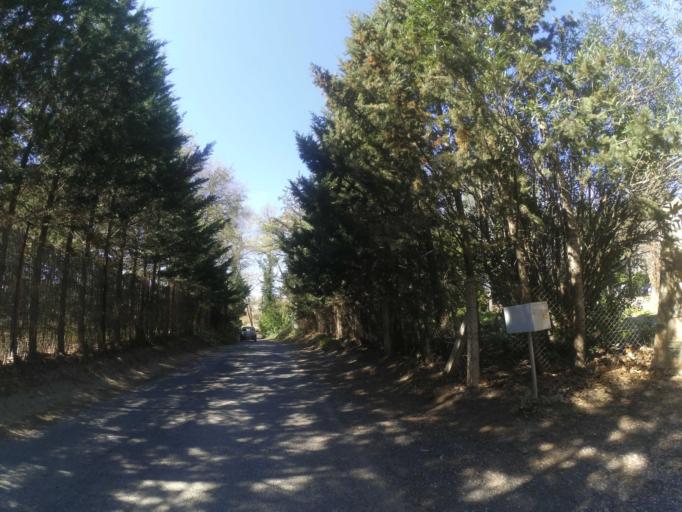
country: FR
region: Languedoc-Roussillon
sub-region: Departement des Pyrenees-Orientales
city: Toulouges
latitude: 42.6737
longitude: 2.8190
